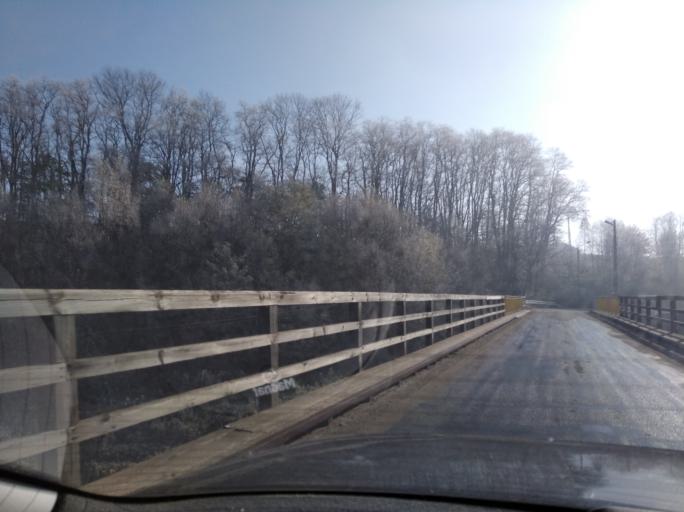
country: PL
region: Subcarpathian Voivodeship
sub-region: Powiat strzyzowski
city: Wysoka Strzyzowska
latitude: 49.8649
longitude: 21.7078
